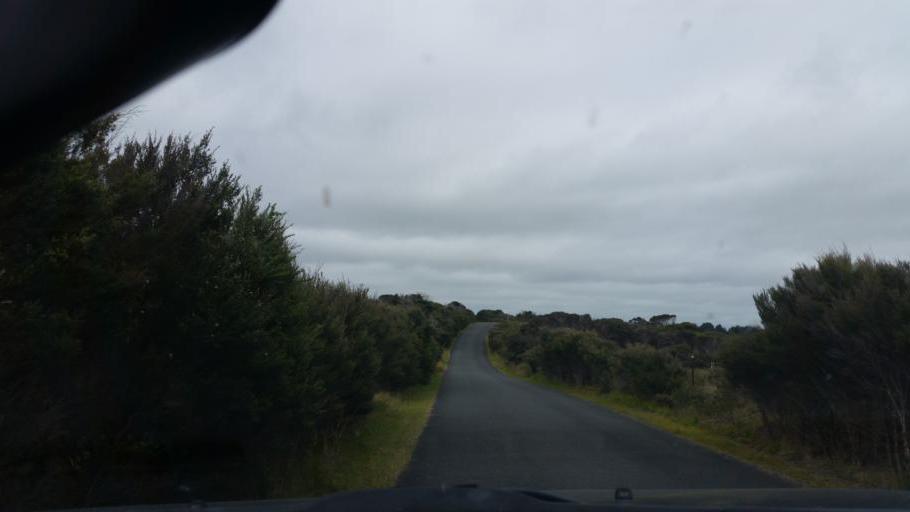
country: NZ
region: Northland
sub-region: Kaipara District
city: Dargaville
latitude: -35.8129
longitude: 173.6485
